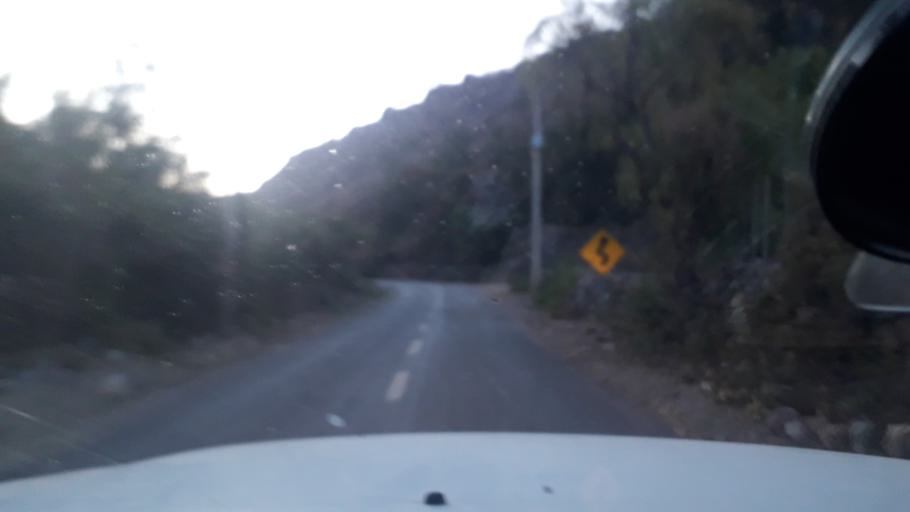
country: CL
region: Valparaiso
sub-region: Provincia de Marga Marga
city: Limache
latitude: -33.1712
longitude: -71.1307
